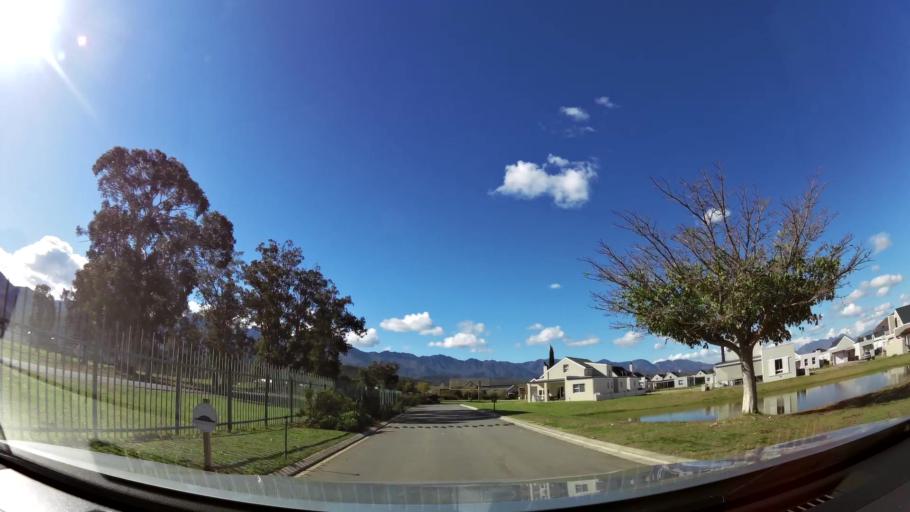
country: ZA
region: Western Cape
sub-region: Cape Winelands District Municipality
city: Ashton
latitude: -33.8103
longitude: 19.8552
